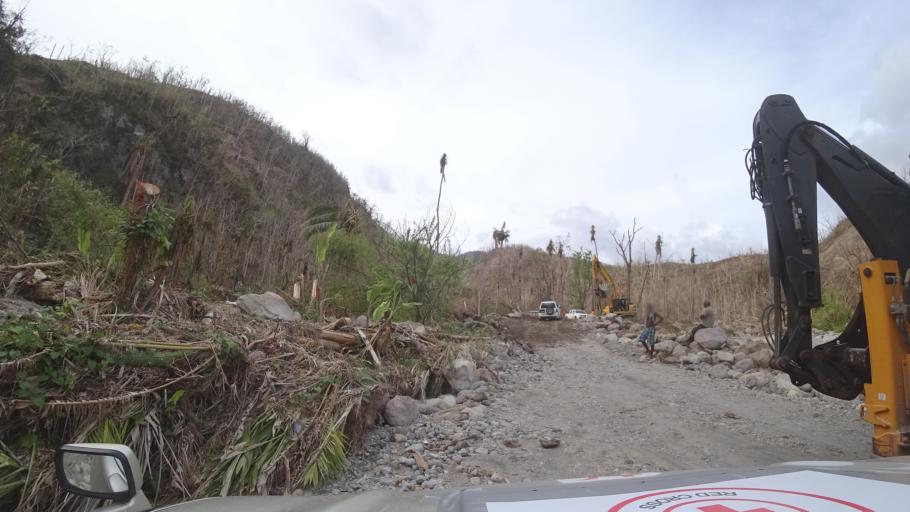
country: DM
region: Saint Patrick
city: Berekua
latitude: 15.2563
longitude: -61.3188
